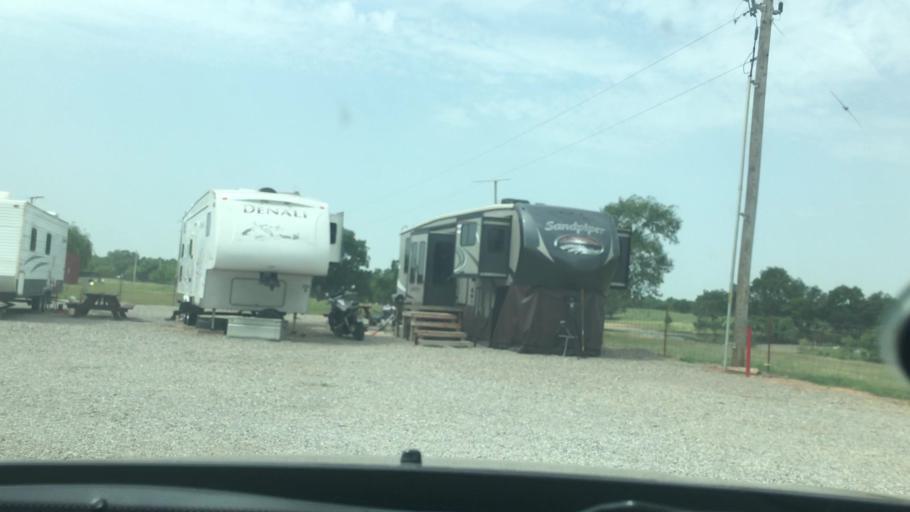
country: US
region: Oklahoma
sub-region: Garvin County
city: Pauls Valley
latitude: 34.8472
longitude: -97.2797
